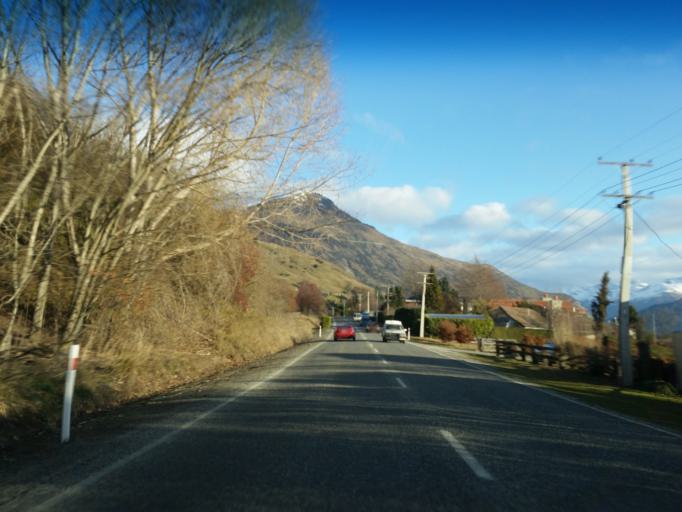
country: NZ
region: Otago
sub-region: Queenstown-Lakes District
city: Arrowtown
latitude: -44.9819
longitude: 168.8171
